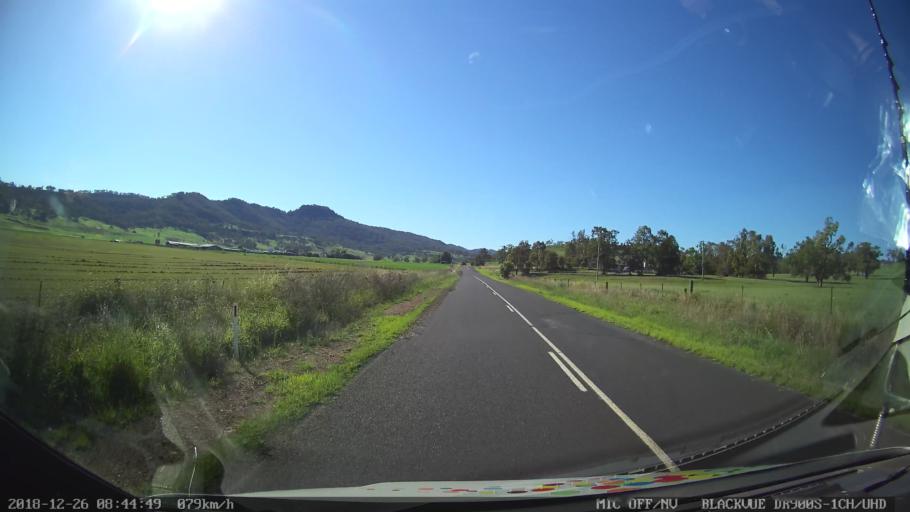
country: AU
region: New South Wales
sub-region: Mid-Western Regional
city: Kandos
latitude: -32.5191
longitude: 150.0816
